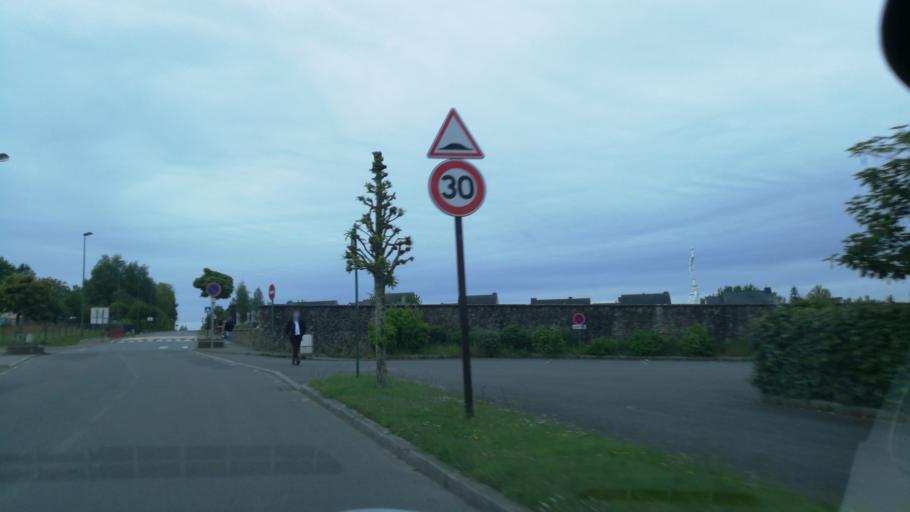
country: FR
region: Brittany
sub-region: Departement d'Ille-et-Vilaine
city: Irodouer
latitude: 48.2469
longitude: -1.9495
